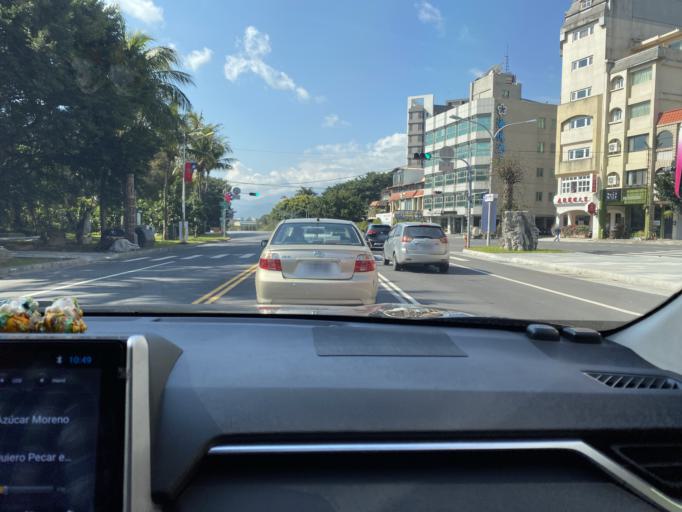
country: TW
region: Taiwan
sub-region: Hualien
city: Hualian
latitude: 23.9820
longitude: 121.6211
